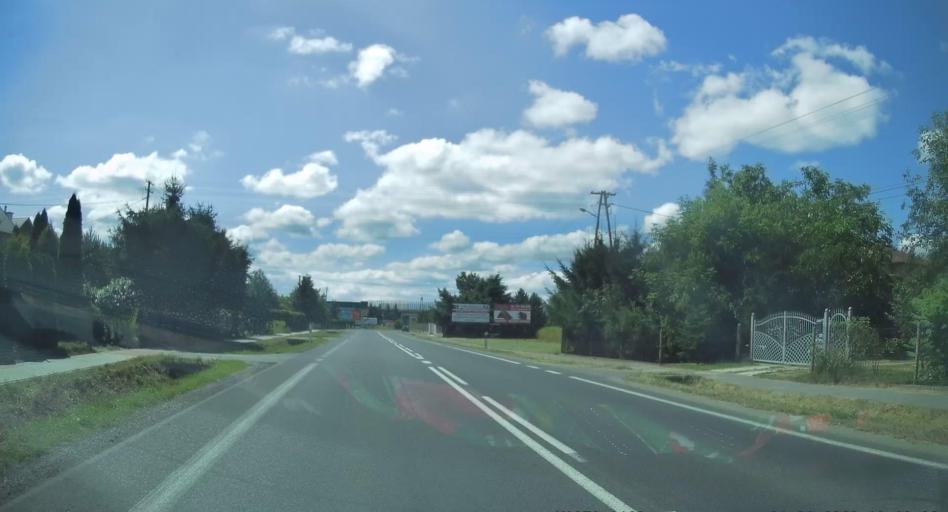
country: PL
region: Subcarpathian Voivodeship
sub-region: Powiat debicki
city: Brzeznica
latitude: 50.0849
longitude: 21.4585
